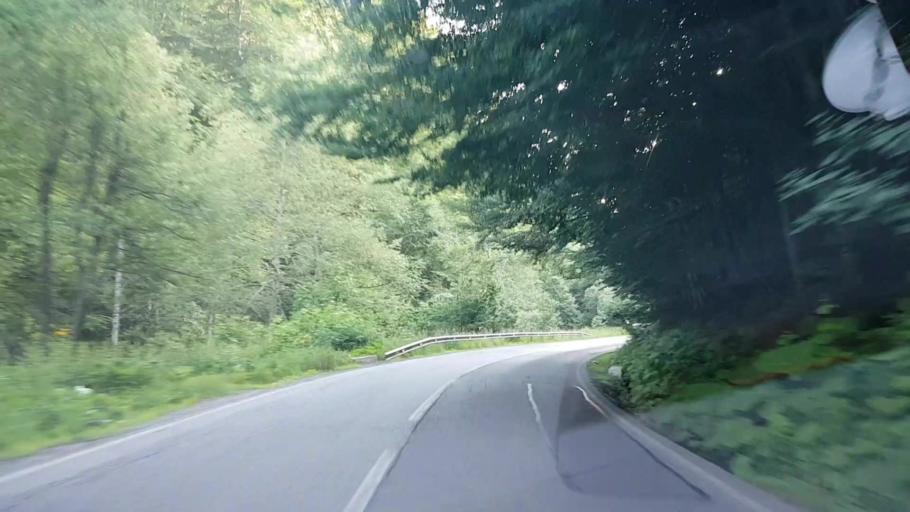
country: RO
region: Harghita
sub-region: Comuna Praid
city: Ocna de Sus
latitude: 46.5802
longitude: 25.2345
